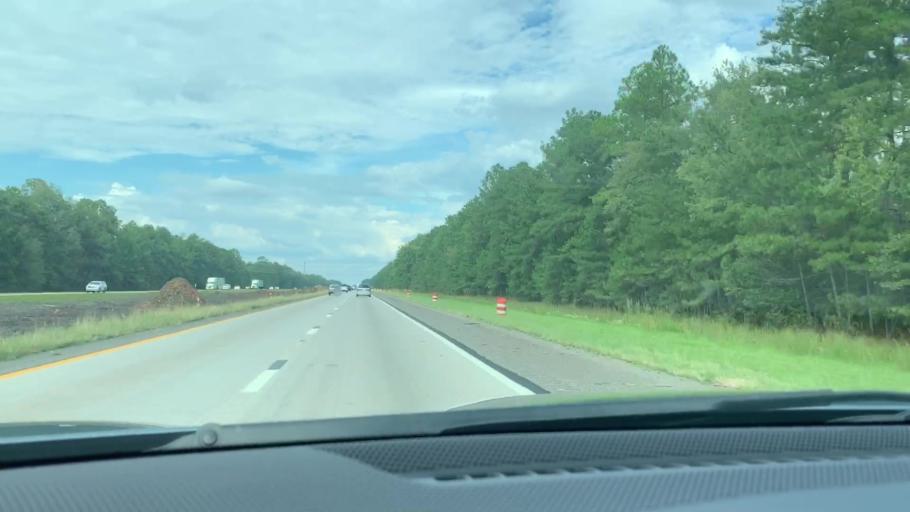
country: US
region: South Carolina
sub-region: Jasper County
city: Hardeeville
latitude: 32.3342
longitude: -81.0508
